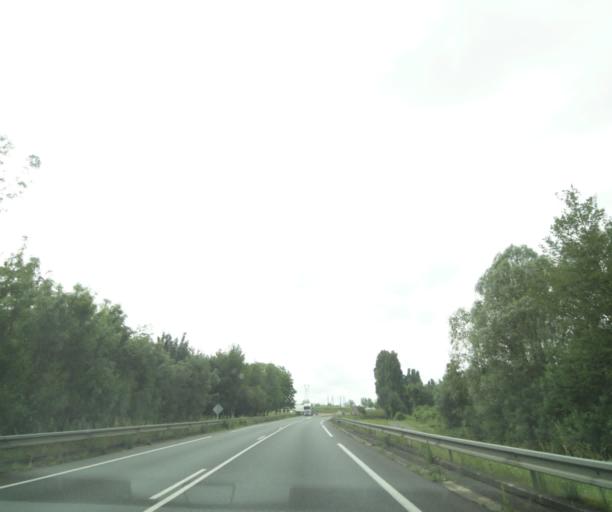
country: FR
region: Pays de la Loire
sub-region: Departement de Maine-et-Loire
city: Distre
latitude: 47.2163
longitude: -0.1160
